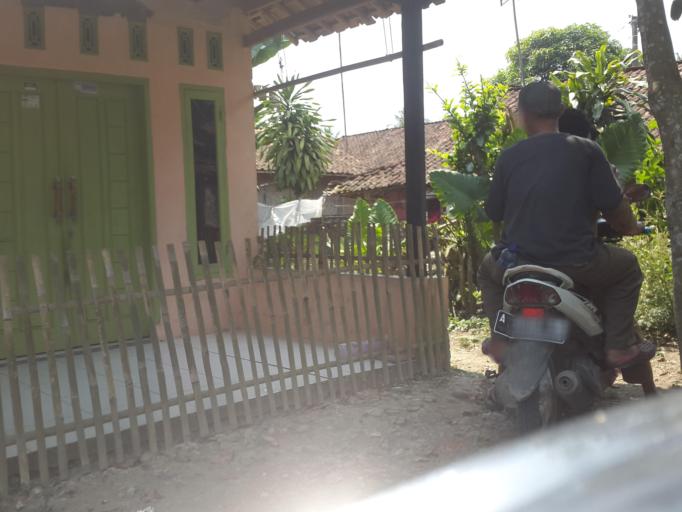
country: ID
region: Banten
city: Guradog
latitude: -6.3650
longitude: 106.4291
